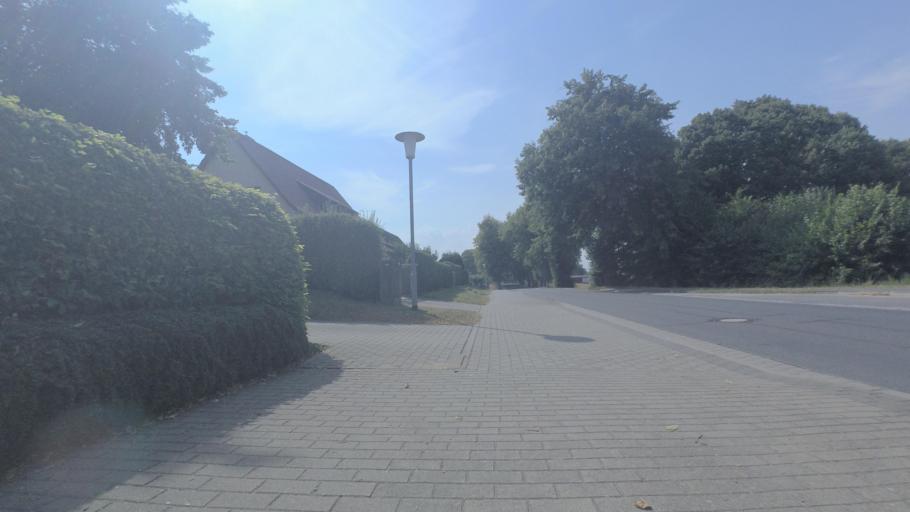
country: DE
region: Mecklenburg-Vorpommern
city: Brandshagen
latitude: 54.2104
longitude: 13.2430
